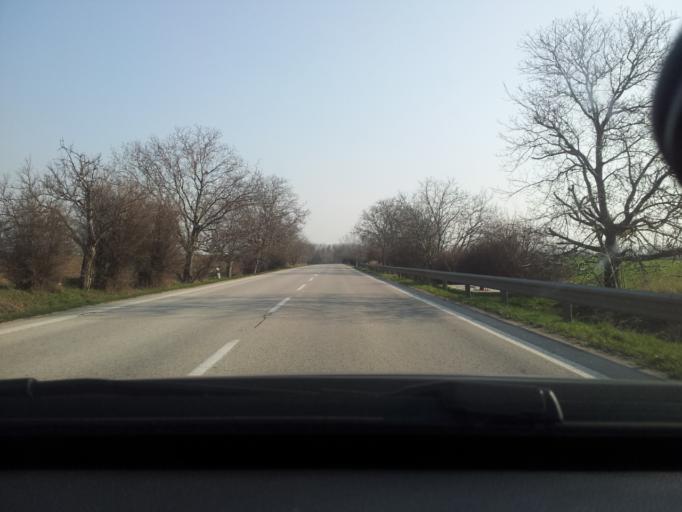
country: SK
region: Trnavsky
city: Leopoldov
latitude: 48.4428
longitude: 17.7052
